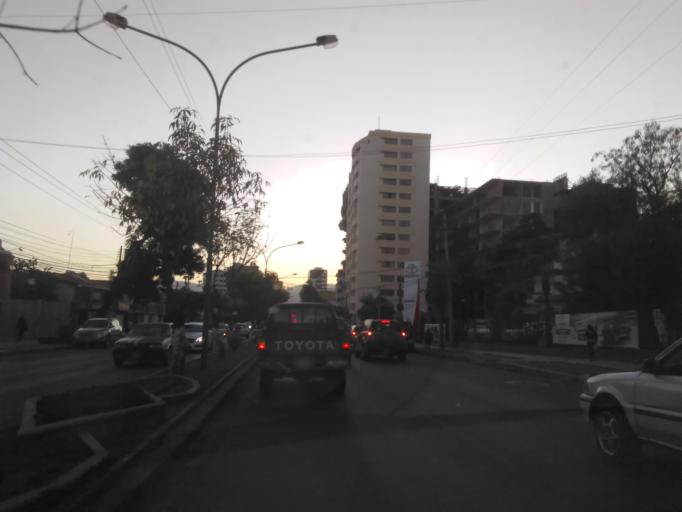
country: BO
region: Cochabamba
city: Cochabamba
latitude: -17.3726
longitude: -66.1597
